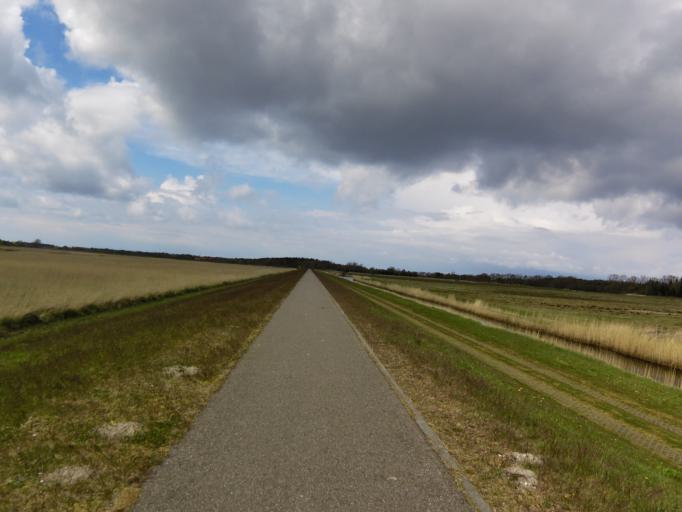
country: DE
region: Mecklenburg-Vorpommern
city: Zingst
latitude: 54.4282
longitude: 12.7280
